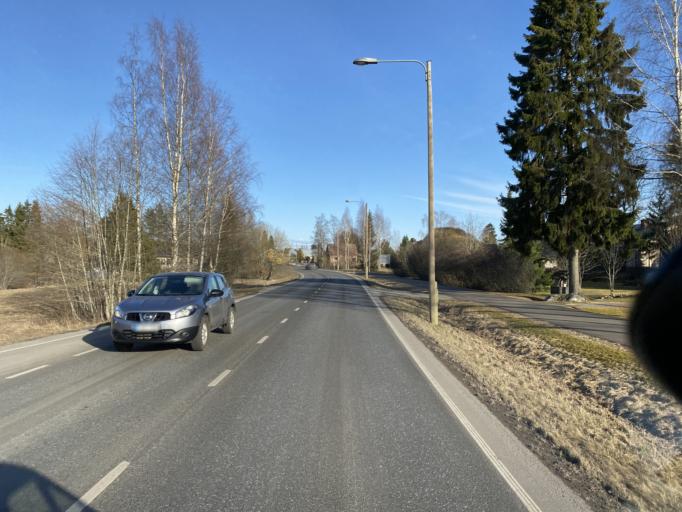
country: FI
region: Satakunta
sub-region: Pori
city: Huittinen
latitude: 61.1801
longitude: 22.7330
